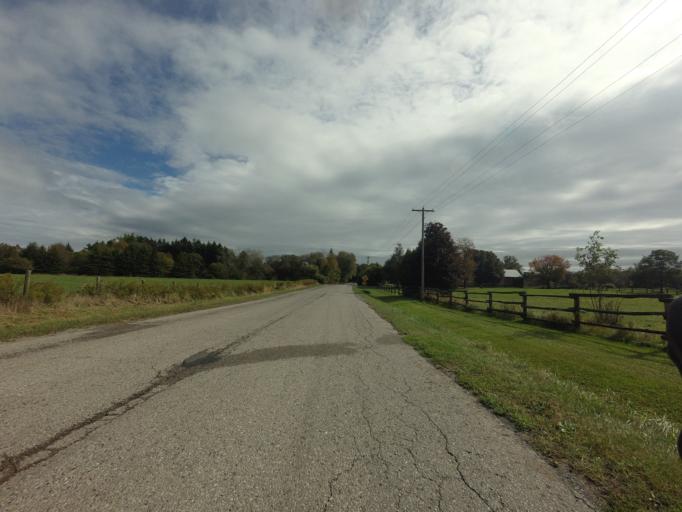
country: CA
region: Ontario
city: Cobourg
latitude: 43.9364
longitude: -78.3700
